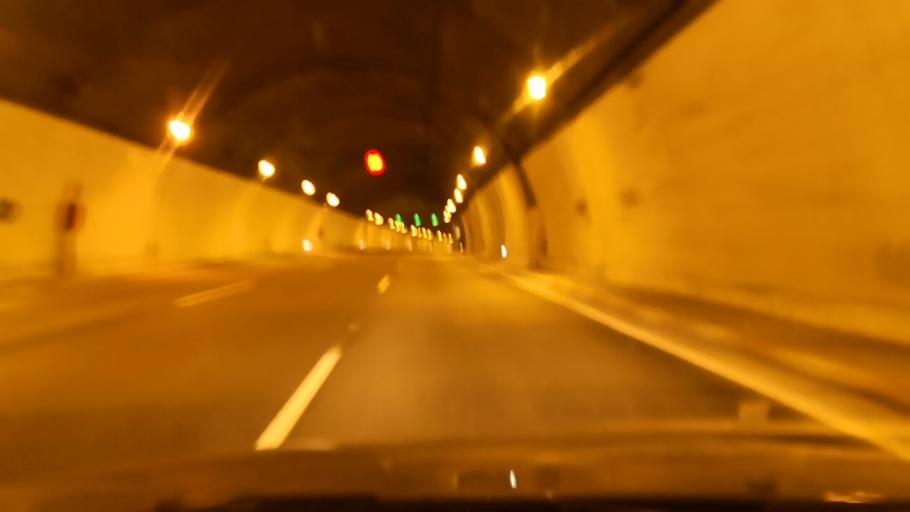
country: ES
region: Castille and Leon
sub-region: Provincia de Zamora
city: Pias
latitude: 42.0374
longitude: -6.9727
